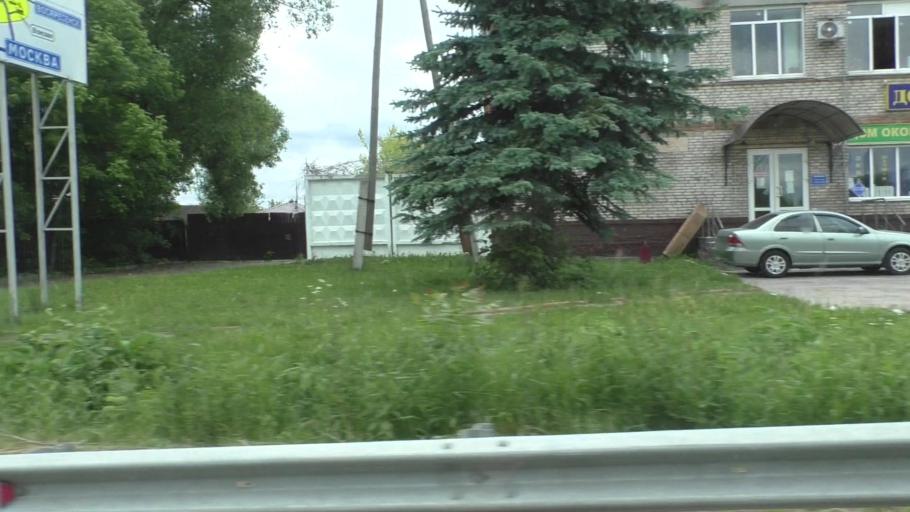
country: RU
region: Moskovskaya
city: Yegor'yevsk
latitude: 55.3965
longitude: 39.0149
